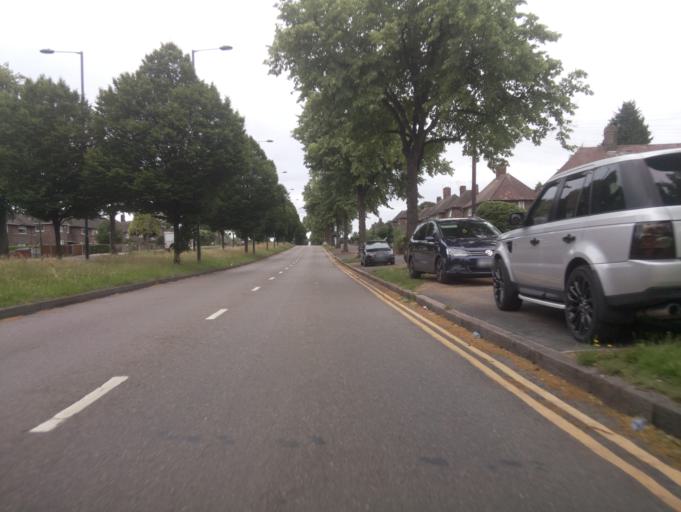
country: GB
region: England
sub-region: Nottingham
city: Nottingham
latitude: 52.9767
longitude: -1.1810
